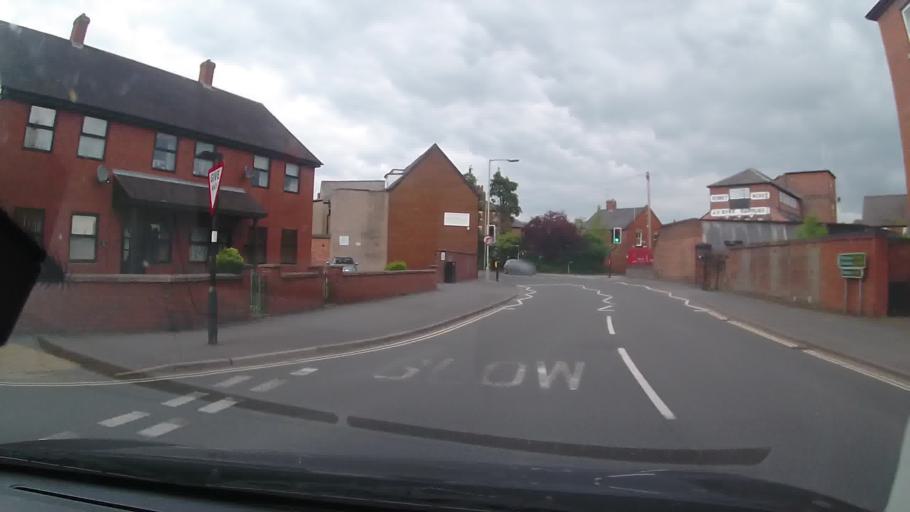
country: GB
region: England
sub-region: Shropshire
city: Ellesmere
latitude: 52.9073
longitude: -2.8958
